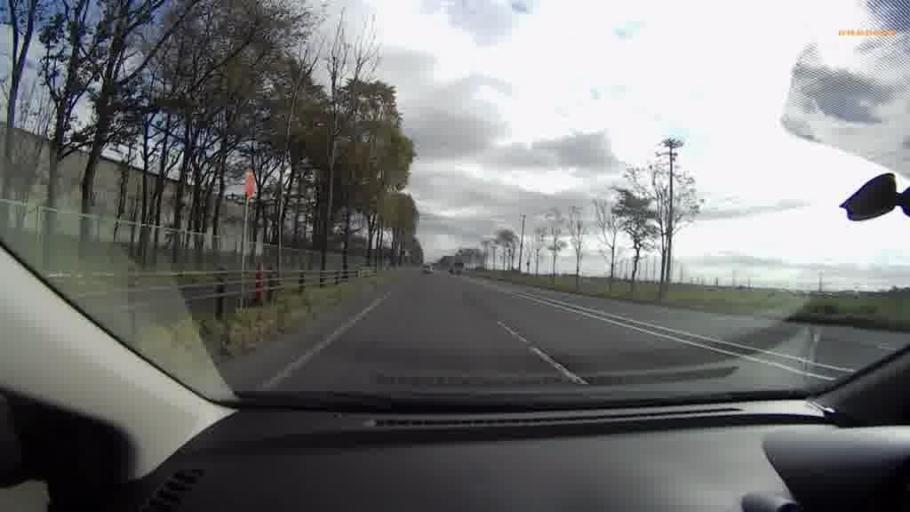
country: JP
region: Hokkaido
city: Kushiro
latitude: 43.0099
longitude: 144.2818
